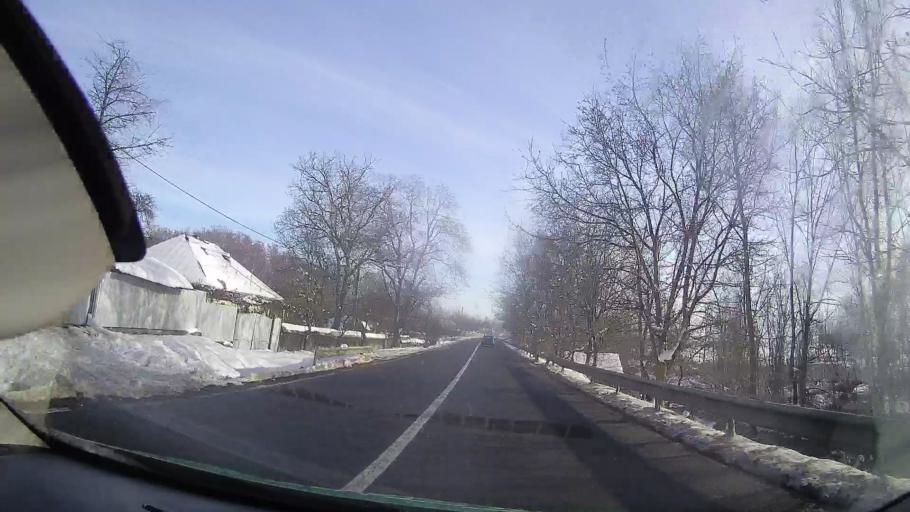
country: RO
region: Neamt
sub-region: Comuna Ghindaoani
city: Ghindaoani
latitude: 47.0730
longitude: 26.3598
